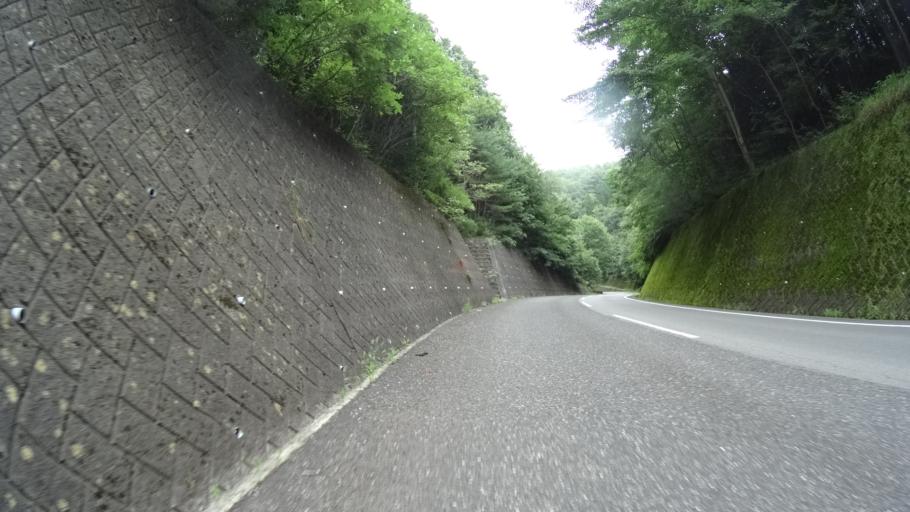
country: JP
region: Yamanashi
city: Nirasaki
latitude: 35.8596
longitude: 138.5217
